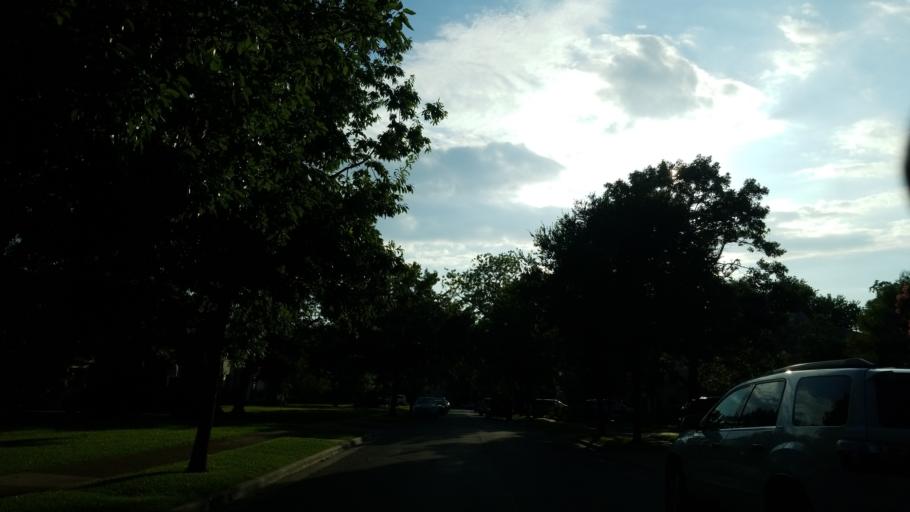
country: US
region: Texas
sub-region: Dallas County
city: University Park
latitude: 32.8473
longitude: -96.7931
